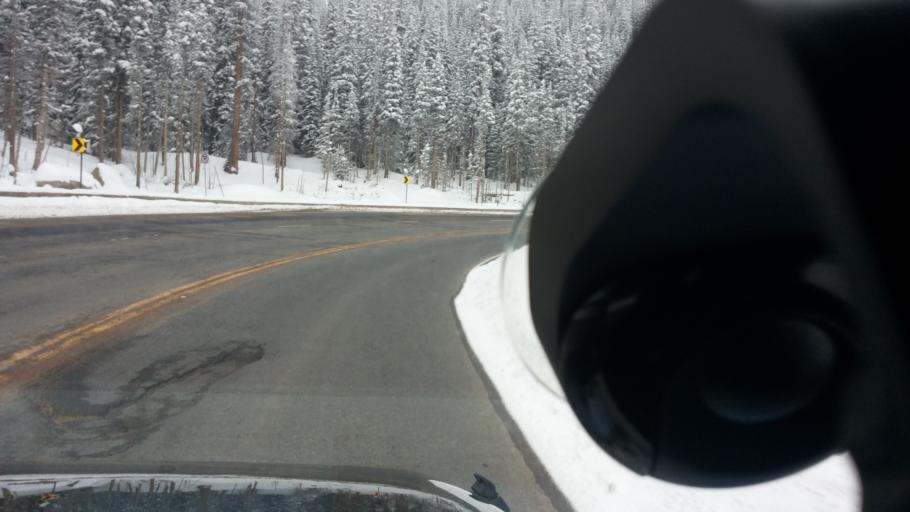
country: US
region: Colorado
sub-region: Clear Creek County
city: Georgetown
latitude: 39.7905
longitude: -105.7816
